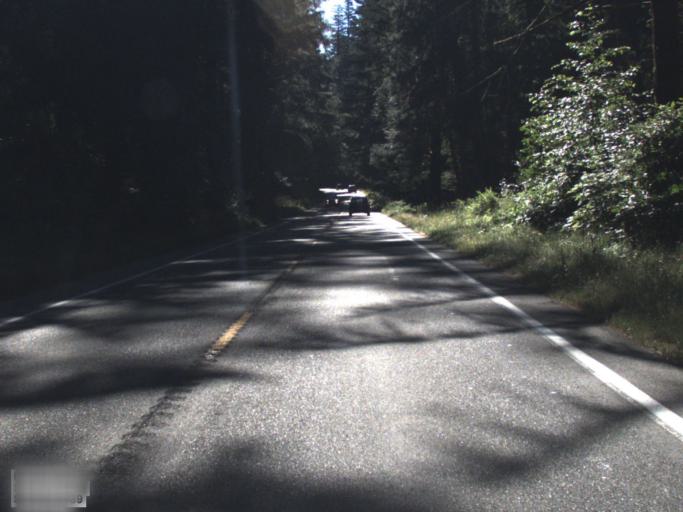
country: US
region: Washington
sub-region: King County
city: Enumclaw
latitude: 47.1549
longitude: -121.7150
